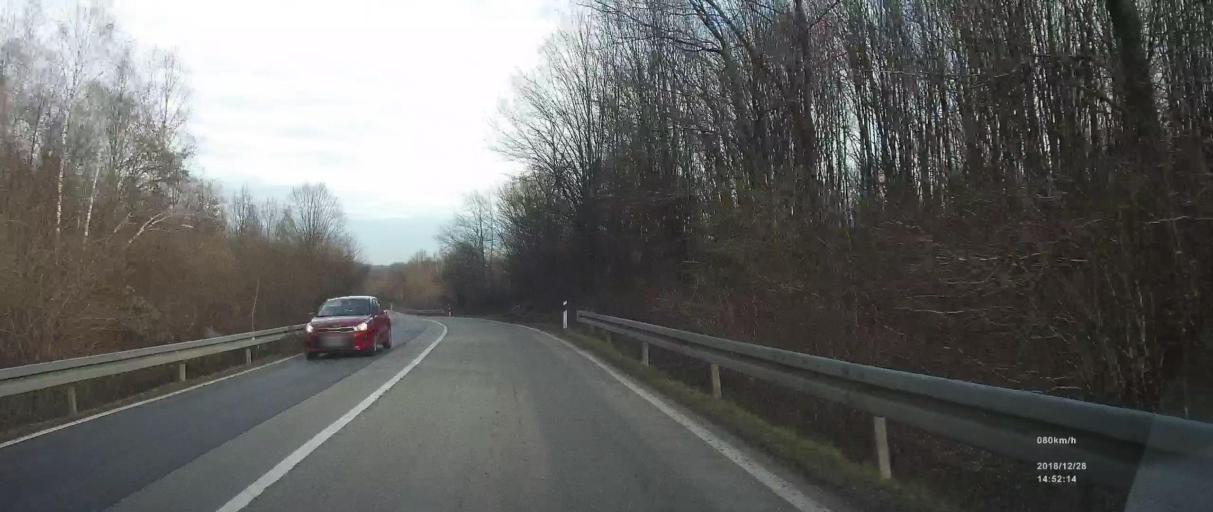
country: HR
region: Karlovacka
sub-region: Grad Karlovac
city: Karlovac
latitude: 45.4451
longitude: 15.3929
